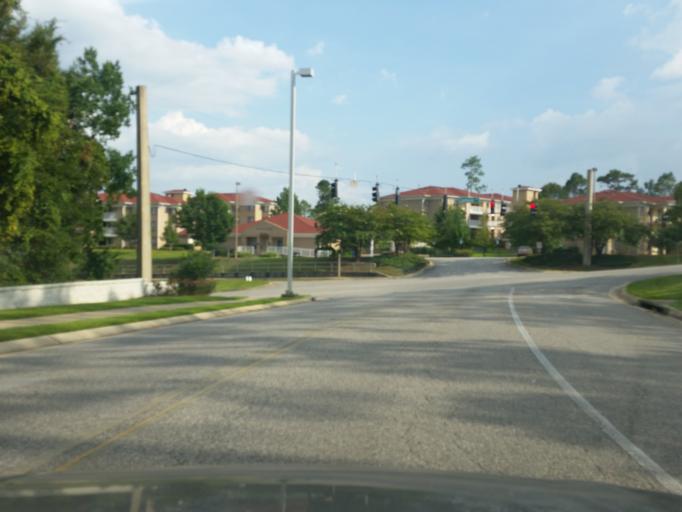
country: US
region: Florida
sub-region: Escambia County
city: Ferry Pass
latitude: 30.5427
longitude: -87.2132
